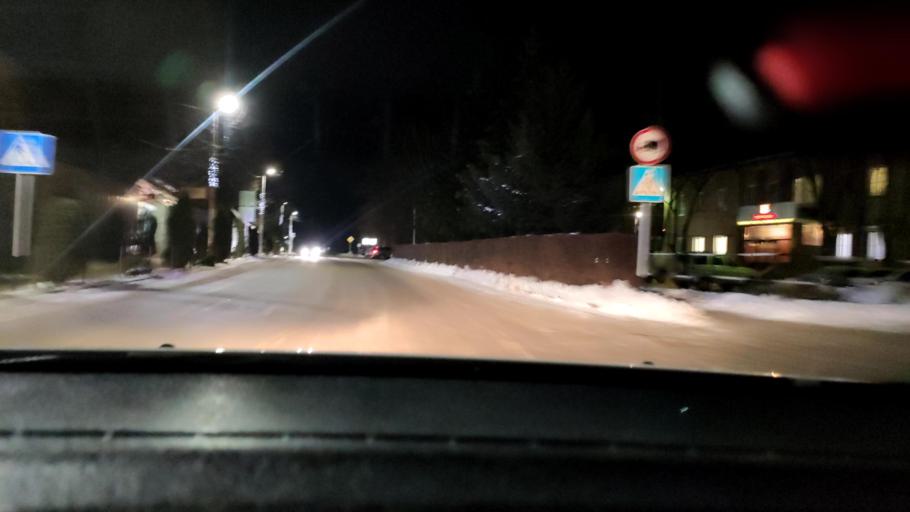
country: RU
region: Voronezj
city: Ramon'
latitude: 51.9142
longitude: 39.3347
